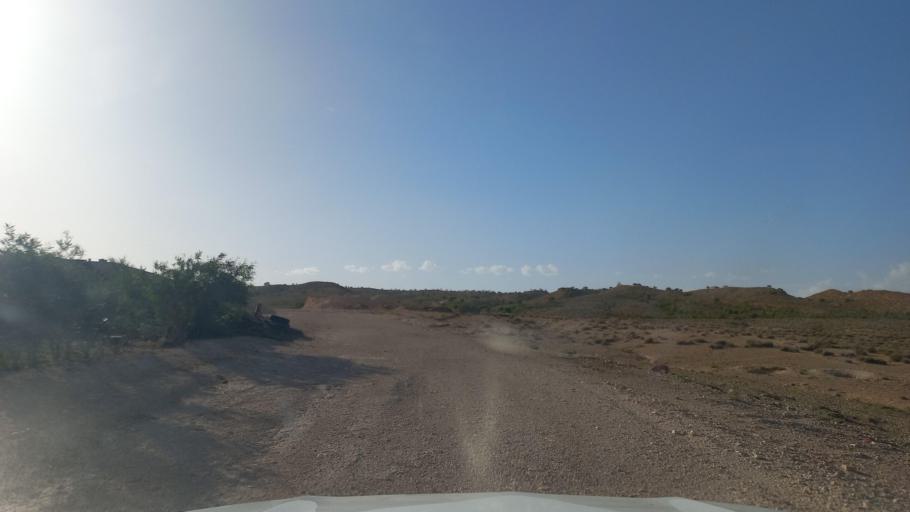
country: TN
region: Al Qasrayn
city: Sbiba
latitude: 35.3646
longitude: 8.9987
